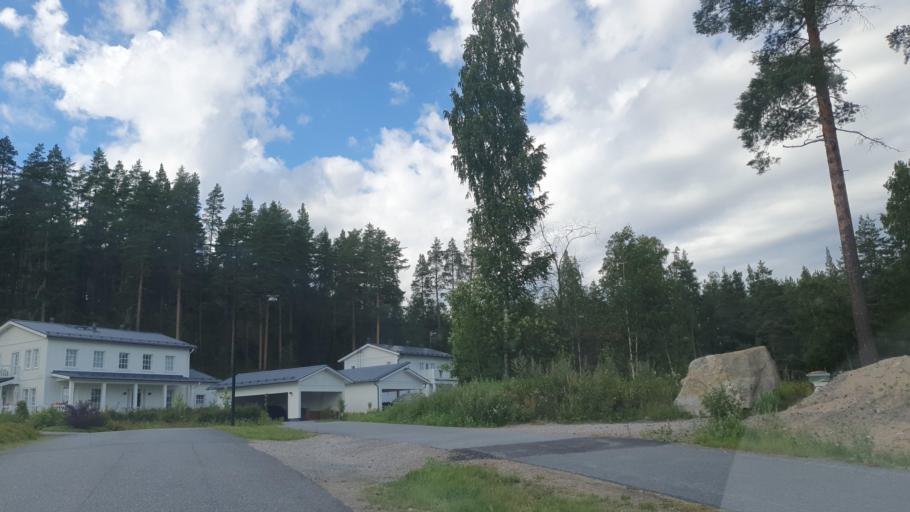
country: FI
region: Central Finland
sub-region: Jyvaeskylae
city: Saeynaetsalo
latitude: 62.1631
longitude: 25.7684
